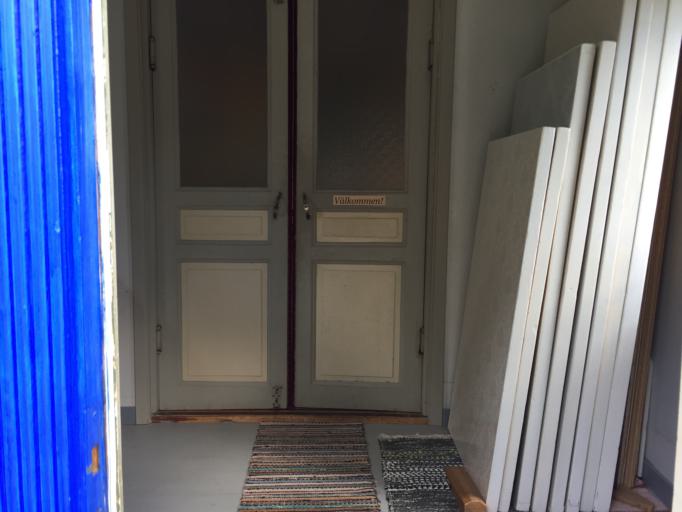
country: SE
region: Soedermanland
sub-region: Vingakers Kommun
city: Vingaker
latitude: 59.0515
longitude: 15.8080
